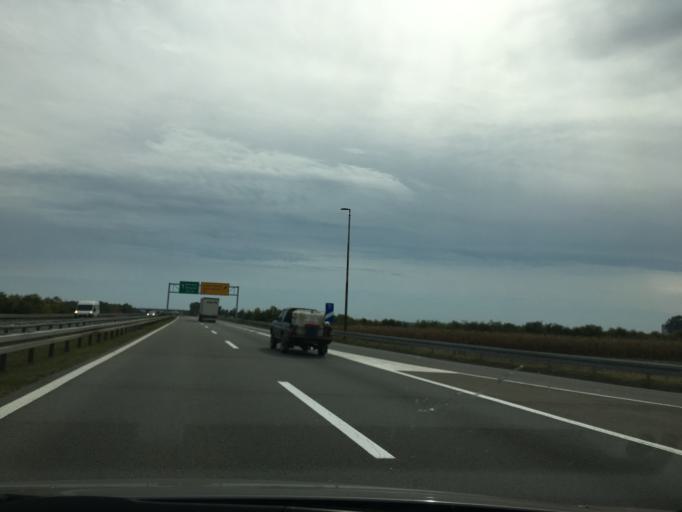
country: RS
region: Autonomna Pokrajina Vojvodina
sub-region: Sremski Okrug
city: Stara Pazova
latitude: 44.9937
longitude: 20.2093
